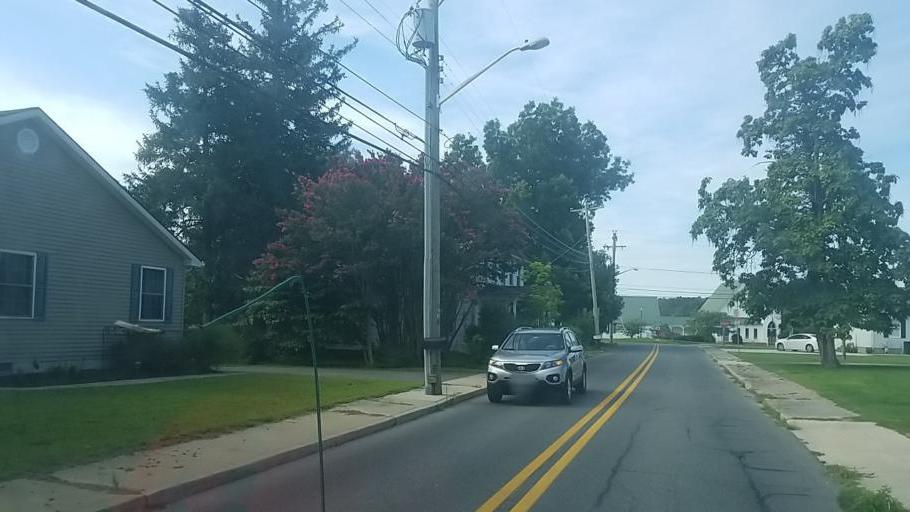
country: US
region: Delaware
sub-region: Sussex County
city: Selbyville
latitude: 38.5169
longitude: -75.2305
